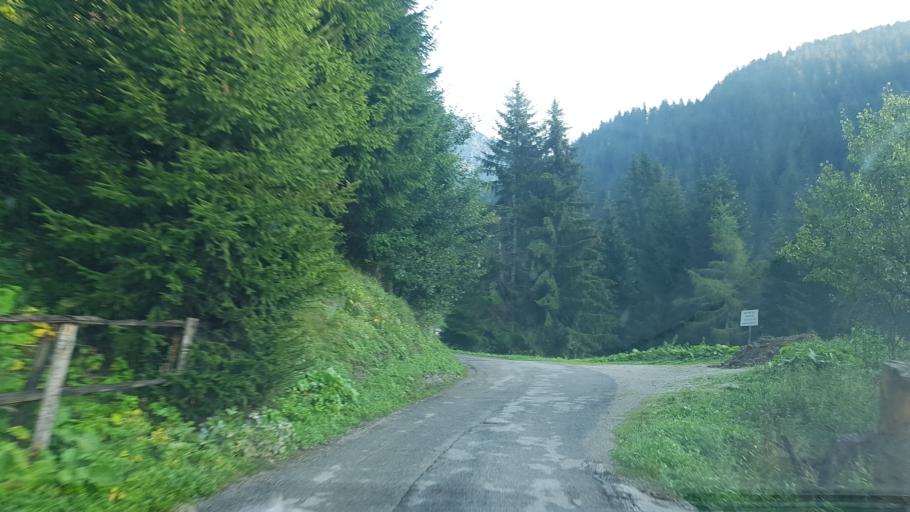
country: IT
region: Veneto
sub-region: Provincia di Belluno
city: San Pietro di Cadore
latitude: 46.5896
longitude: 12.5807
